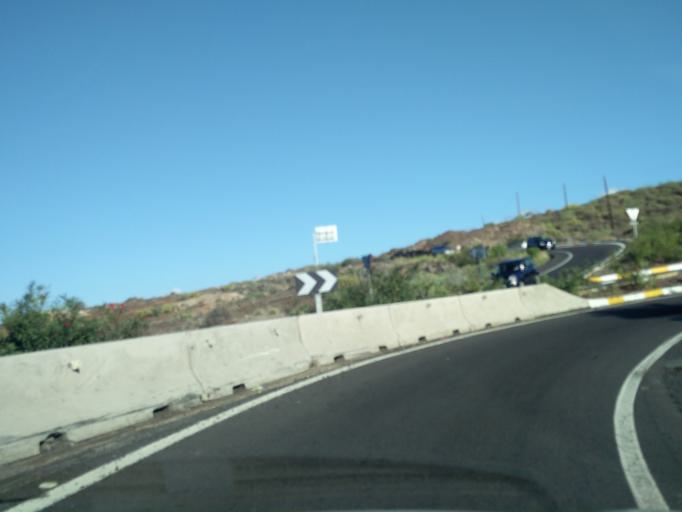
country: ES
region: Canary Islands
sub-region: Provincia de Santa Cruz de Tenerife
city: Playa de las Americas
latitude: 28.0648
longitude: -16.7117
